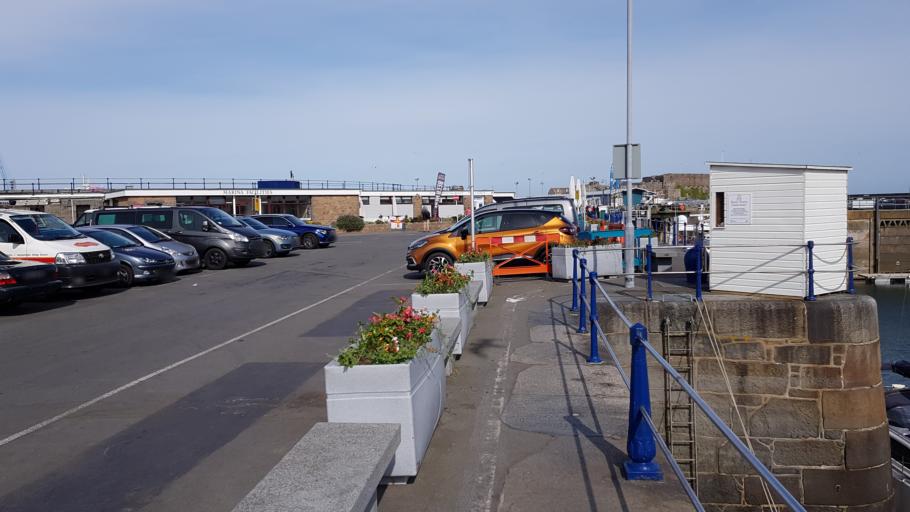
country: GG
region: St Peter Port
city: Saint Peter Port
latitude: 49.4543
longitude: -2.5345
